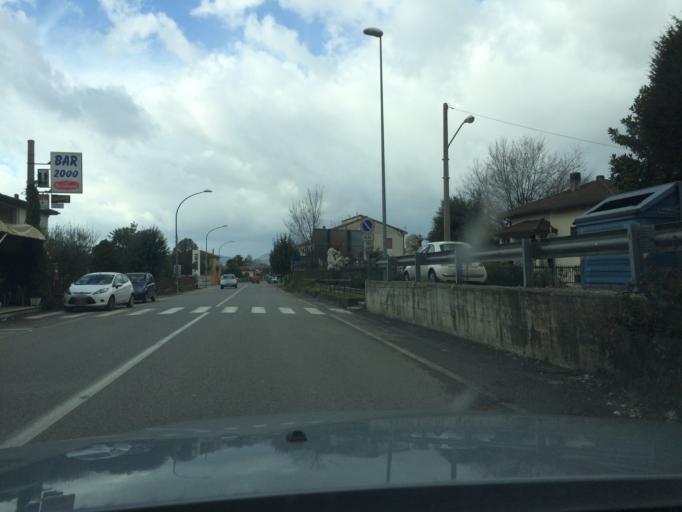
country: IT
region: Umbria
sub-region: Provincia di Terni
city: Terni
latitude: 42.5455
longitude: 12.6085
